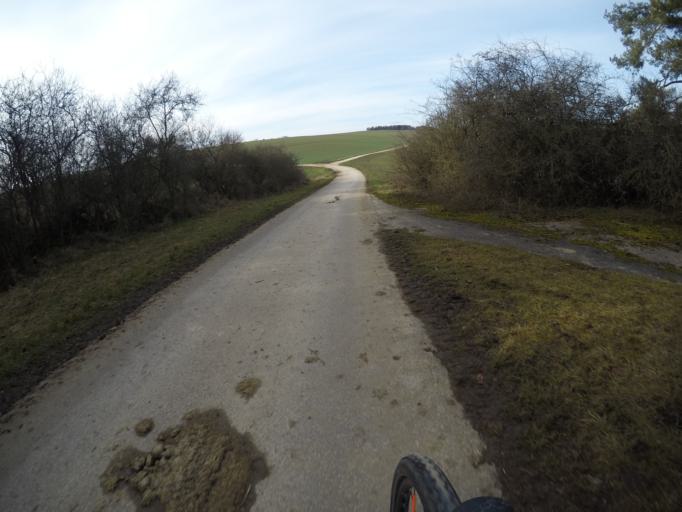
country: DE
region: Baden-Wuerttemberg
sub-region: Karlsruhe Region
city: Ostelsheim
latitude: 48.7081
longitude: 8.8676
